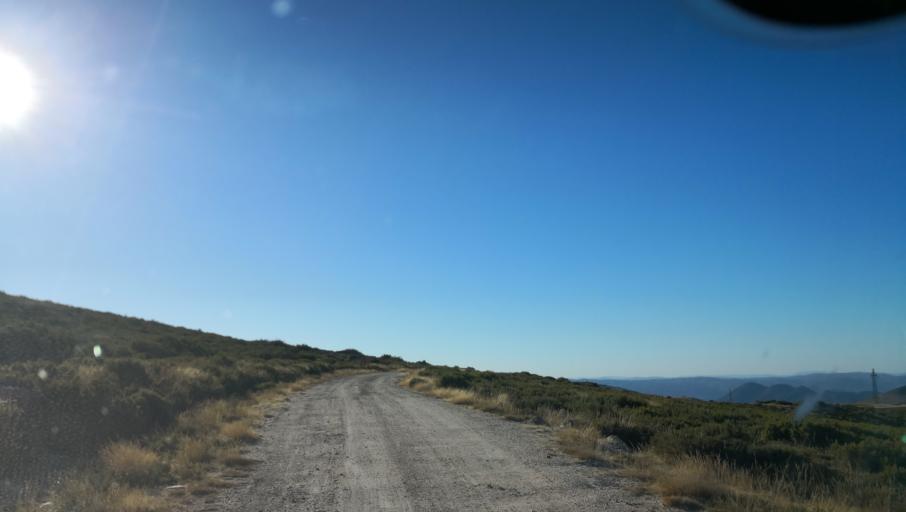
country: PT
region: Vila Real
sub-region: Vila Real
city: Vila Real
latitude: 41.3559
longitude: -7.7711
